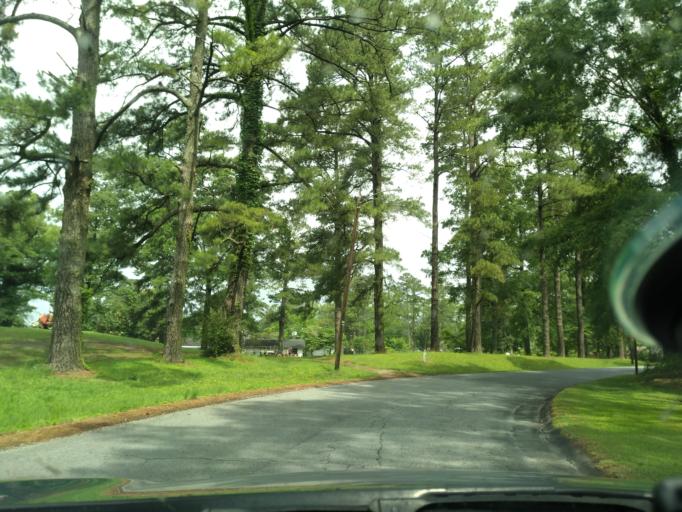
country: US
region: North Carolina
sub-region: Washington County
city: Plymouth
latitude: 35.8561
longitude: -76.7581
